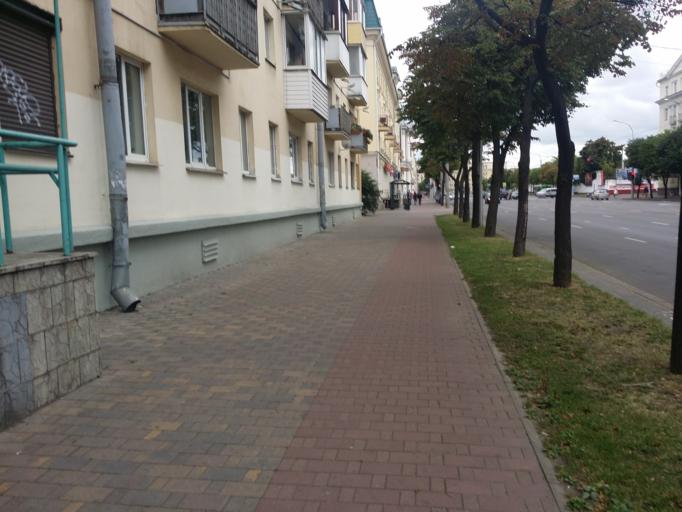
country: BY
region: Minsk
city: Minsk
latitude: 53.9144
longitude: 27.5742
